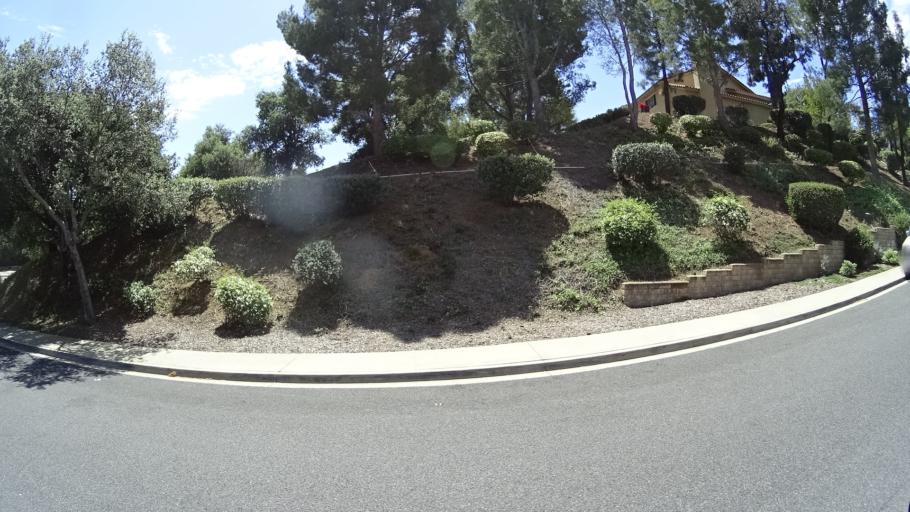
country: US
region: California
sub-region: Ventura County
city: Casa Conejo
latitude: 34.1811
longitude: -118.9038
